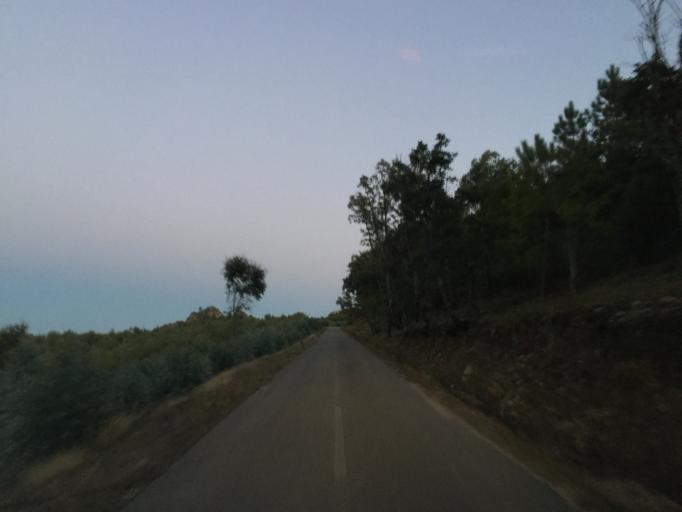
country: PT
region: Portalegre
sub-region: Castelo de Vide
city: Castelo de Vide
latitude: 39.4066
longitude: -7.4607
